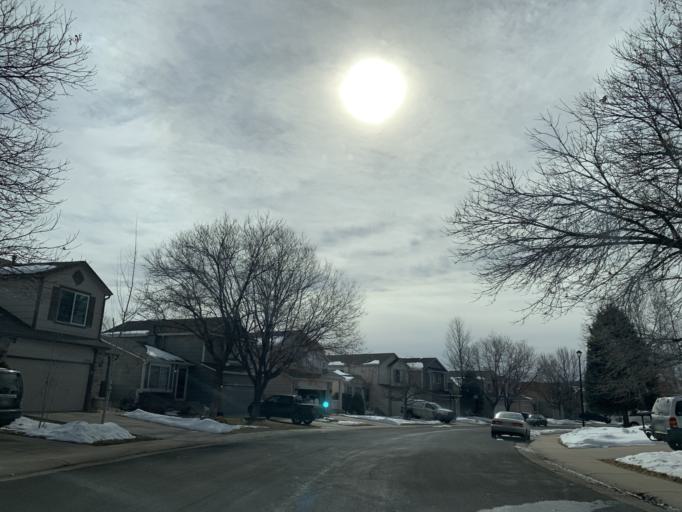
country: US
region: Colorado
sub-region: Douglas County
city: Carriage Club
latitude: 39.5407
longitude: -104.9287
